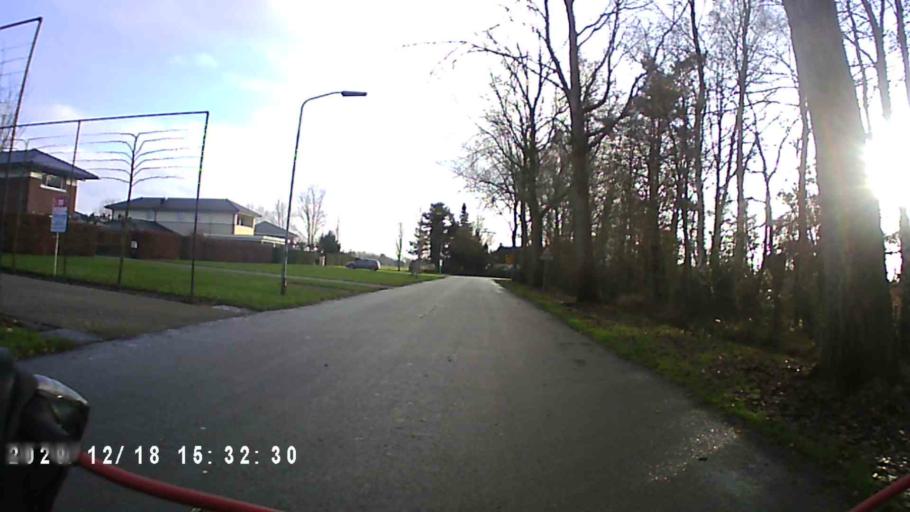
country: NL
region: Groningen
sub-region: Gemeente Hoogezand-Sappemeer
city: Hoogezand
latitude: 53.1388
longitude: 6.7156
